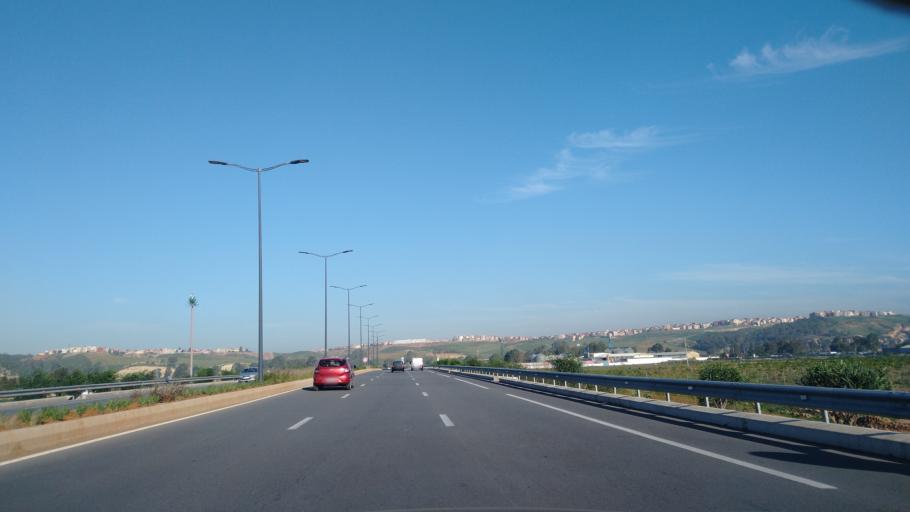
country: MA
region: Rabat-Sale-Zemmour-Zaer
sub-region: Rabat
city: Rabat
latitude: 34.0094
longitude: -6.7990
